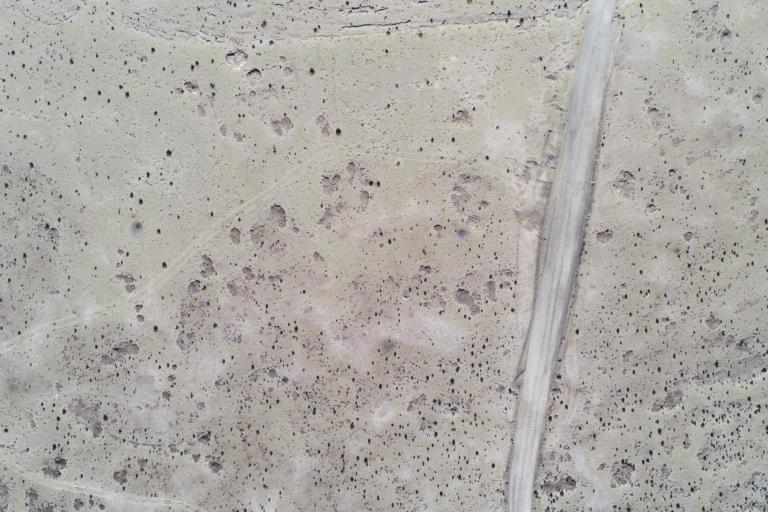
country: BO
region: Potosi
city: Colchani
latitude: -20.3521
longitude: -66.8977
